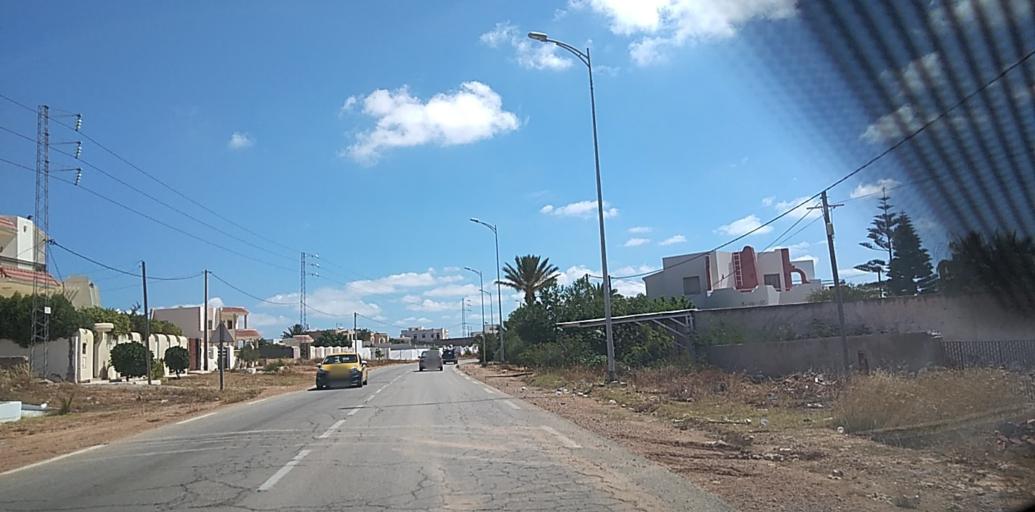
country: TN
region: Safaqis
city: Al Qarmadah
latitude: 34.6758
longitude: 11.1486
